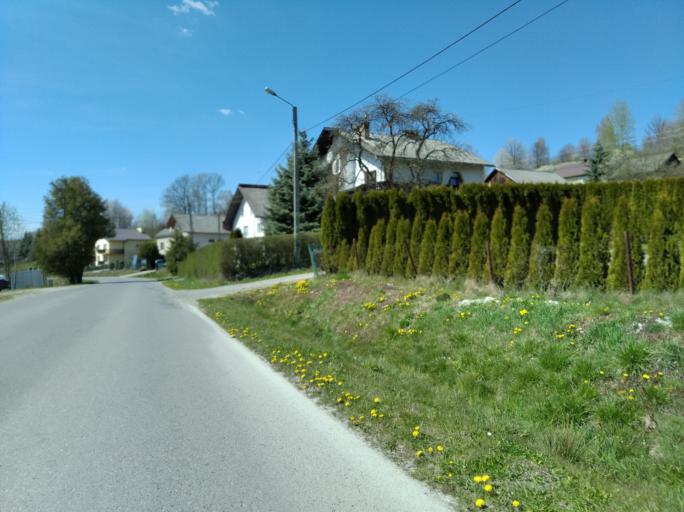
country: PL
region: Subcarpathian Voivodeship
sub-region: Powiat brzozowski
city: Domaradz
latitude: 49.7916
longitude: 21.9757
